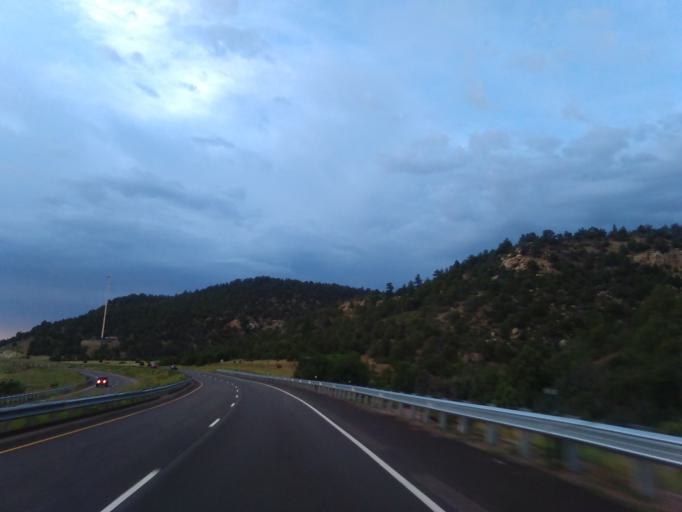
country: US
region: Colorado
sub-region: Las Animas County
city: Trinidad
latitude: 37.0937
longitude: -104.5189
